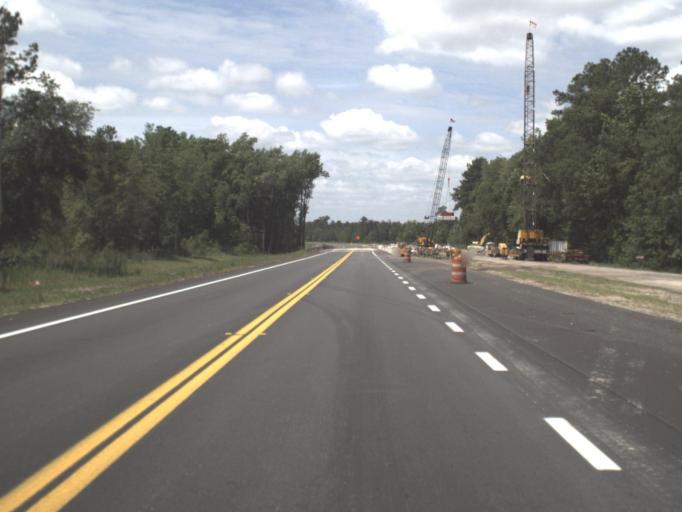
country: US
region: Florida
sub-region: Nassau County
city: Nassau Village-Ratliff
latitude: 30.4778
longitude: -81.9030
